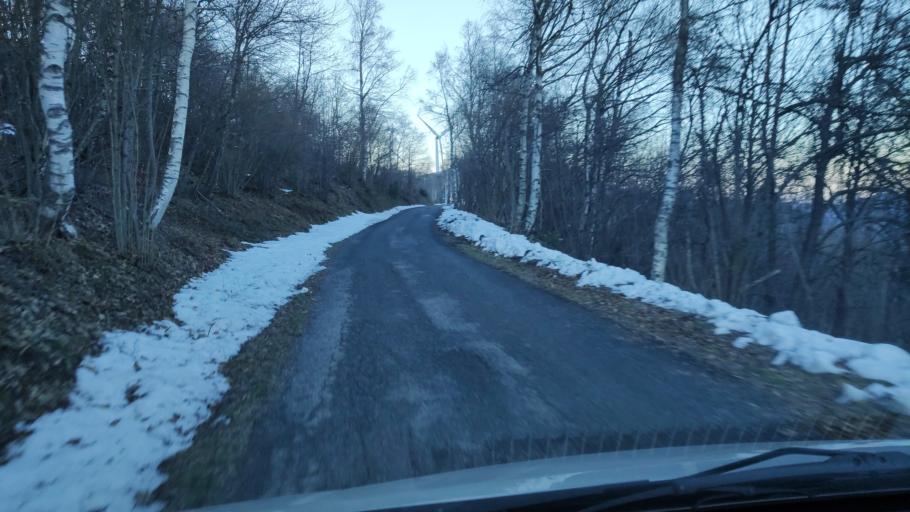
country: IT
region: Piedmont
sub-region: Provincia di Cuneo
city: Viola
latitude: 44.2744
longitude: 7.9942
